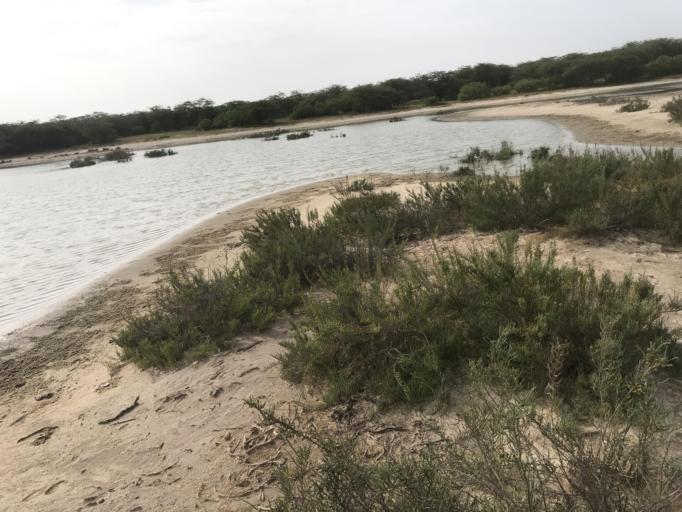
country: SN
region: Saint-Louis
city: Saint-Louis
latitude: 15.9269
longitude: -16.4649
